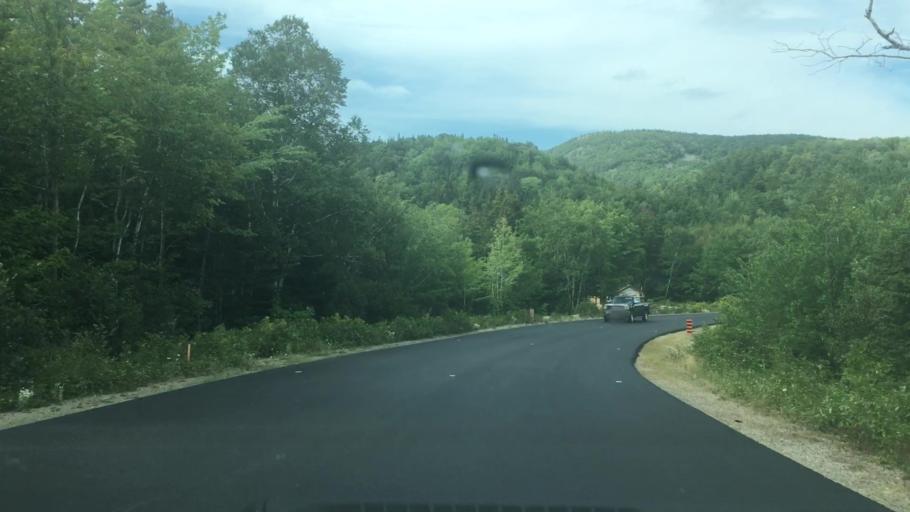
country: CA
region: Nova Scotia
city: Sydney Mines
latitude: 46.5437
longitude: -60.4152
